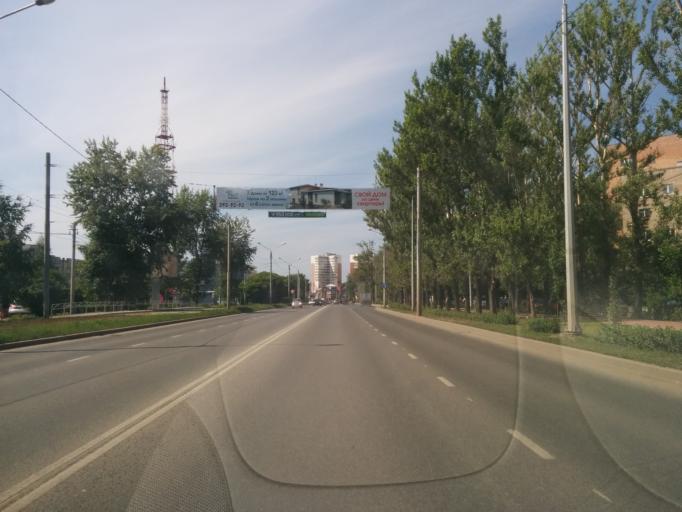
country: RU
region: Perm
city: Perm
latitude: 57.9915
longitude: 56.2943
